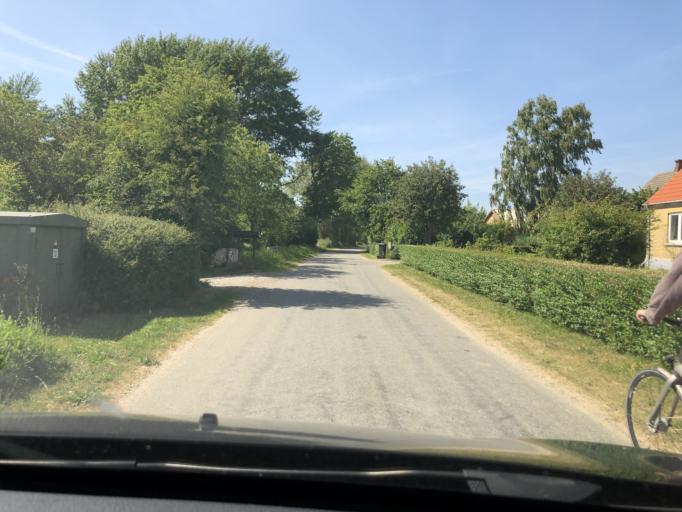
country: DK
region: South Denmark
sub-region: AEro Kommune
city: AEroskobing
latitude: 54.8926
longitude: 10.2982
